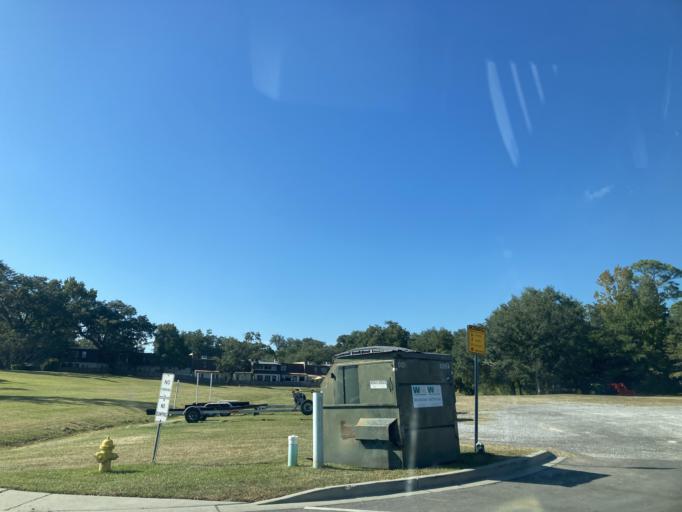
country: US
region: Mississippi
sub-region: Jackson County
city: Ocean Springs
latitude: 30.4038
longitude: -88.8236
